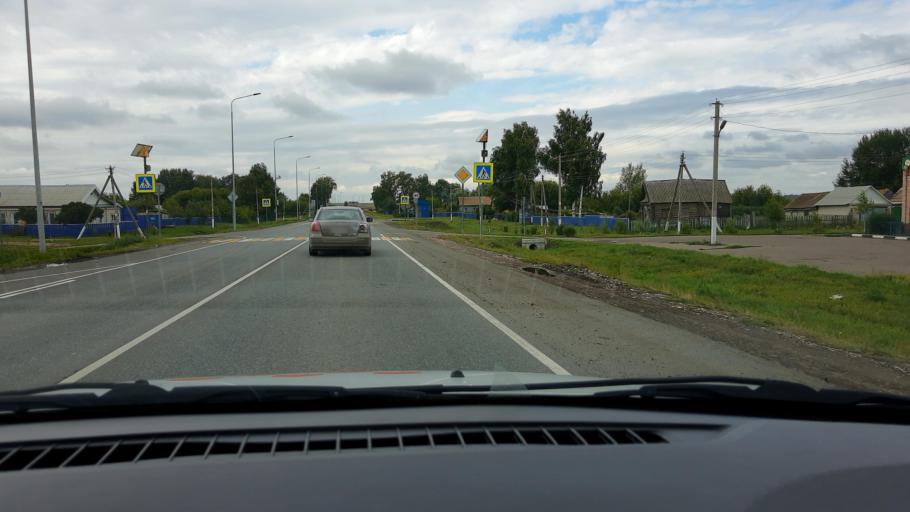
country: RU
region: Tatarstan
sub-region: Alekseyevskiy Rayon
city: Alekseyevskoye
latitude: 55.3098
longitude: 50.3032
